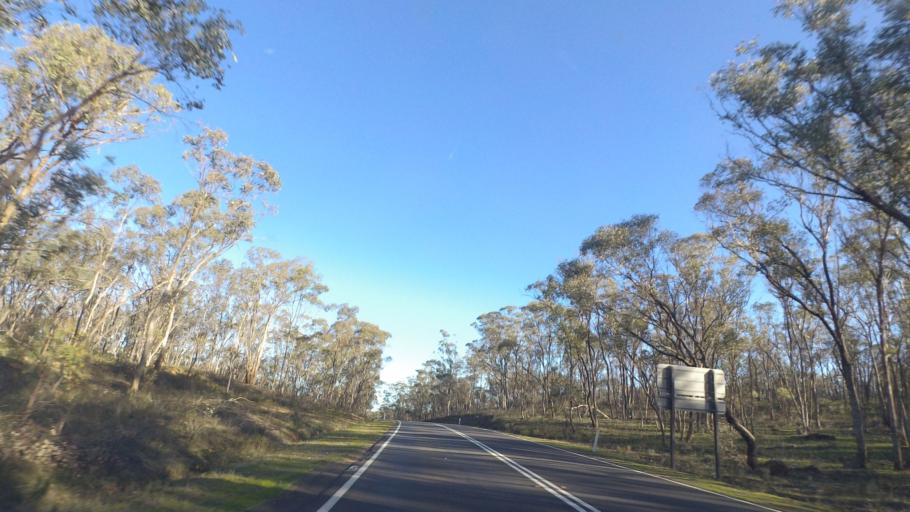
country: AU
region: Victoria
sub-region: Greater Bendigo
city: Kennington
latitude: -36.9122
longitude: 144.4927
